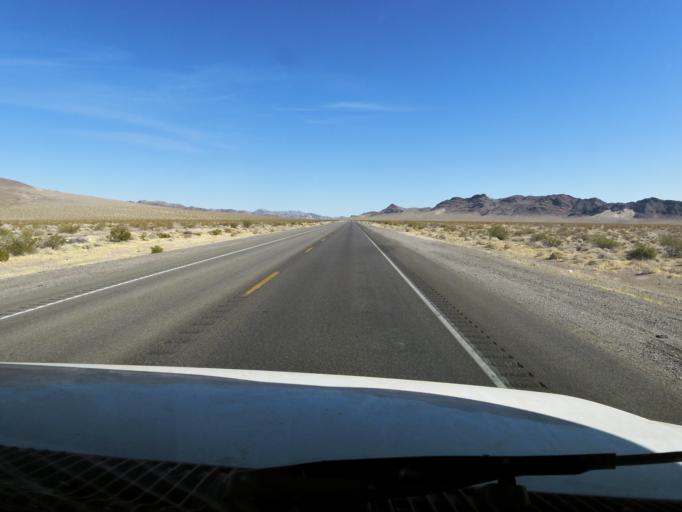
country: US
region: Nevada
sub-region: Nye County
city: Beatty
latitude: 36.6364
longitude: -116.3705
